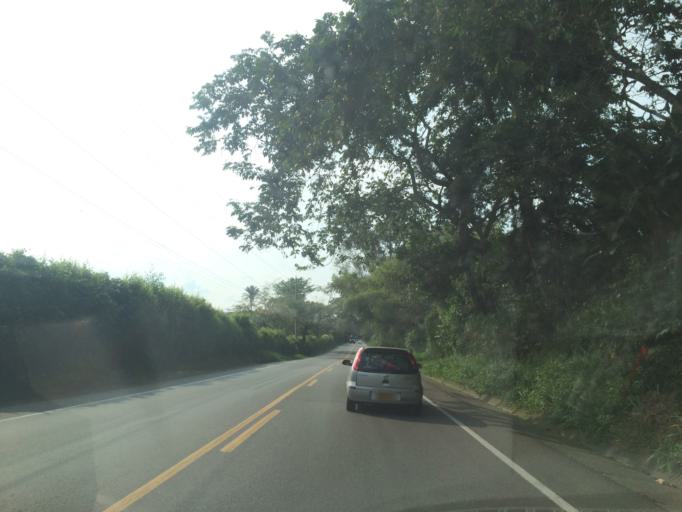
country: CO
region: Quindio
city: La Tebaida
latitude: 4.4478
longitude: -75.8092
